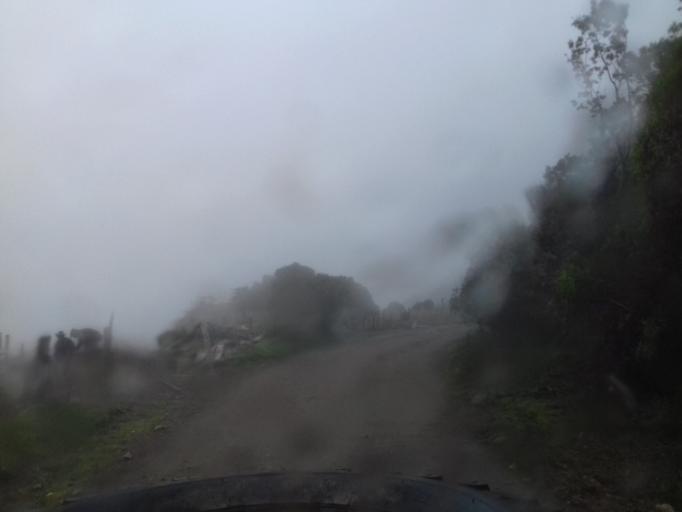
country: CO
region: Tolima
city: Murillo
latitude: 4.8898
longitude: -75.2566
